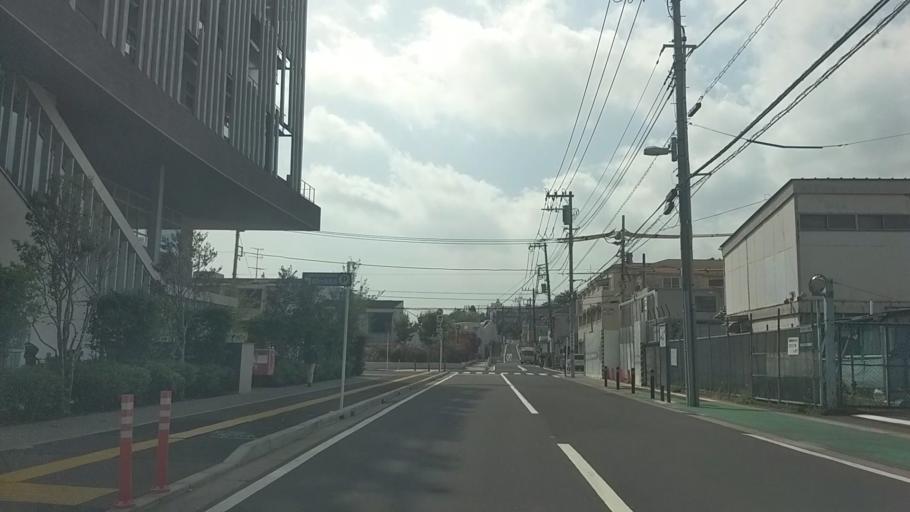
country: JP
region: Kanagawa
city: Yokohama
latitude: 35.4010
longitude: 139.5917
